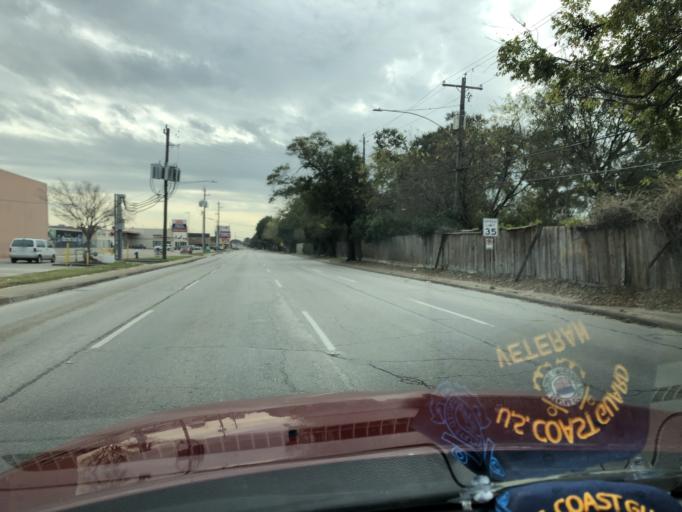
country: US
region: Texas
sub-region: Harris County
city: Houston
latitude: 29.7896
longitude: -95.4119
